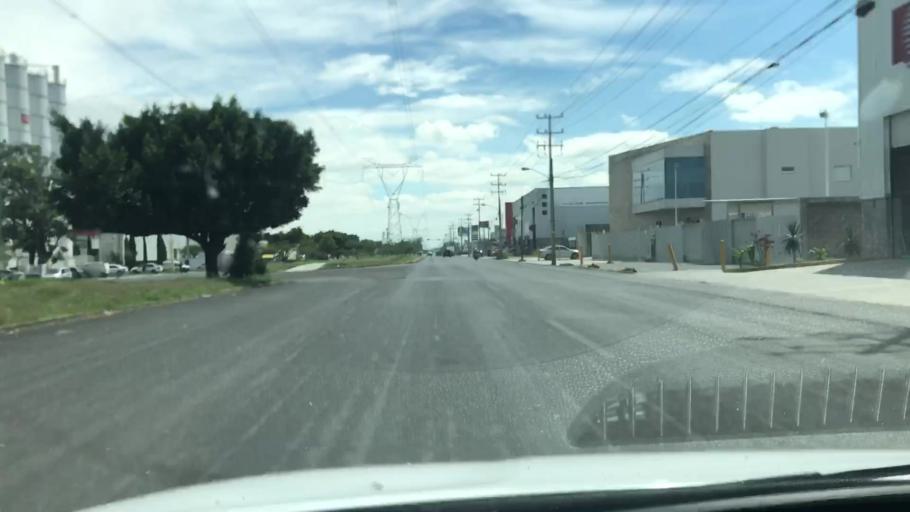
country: MX
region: Guanajuato
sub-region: Celaya
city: La Trinidad
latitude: 20.5499
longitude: -100.7973
